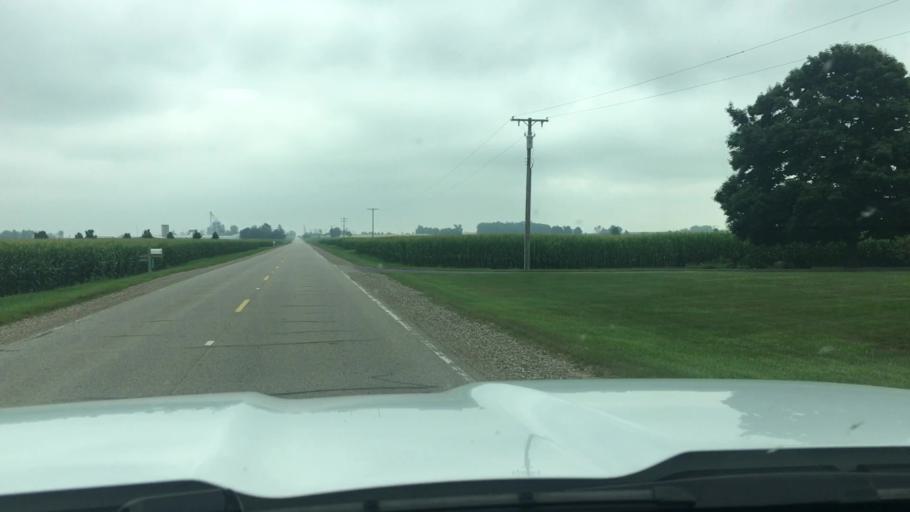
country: US
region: Michigan
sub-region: Sanilac County
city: Brown City
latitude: 43.2556
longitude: -83.0451
